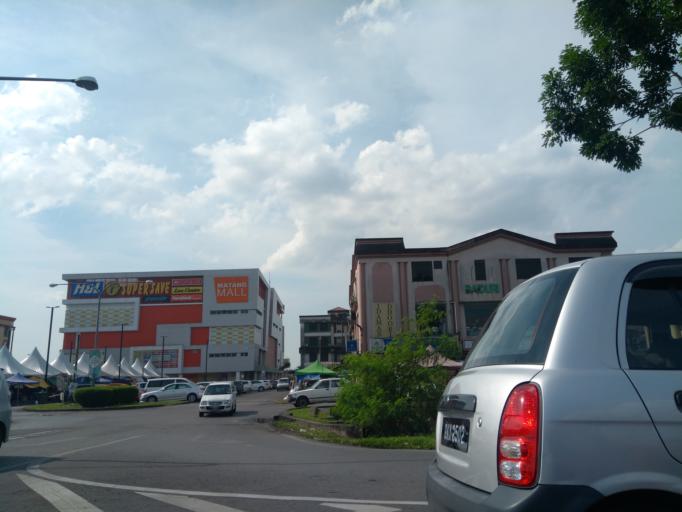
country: MY
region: Sarawak
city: Kuching
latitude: 1.5734
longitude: 110.2964
